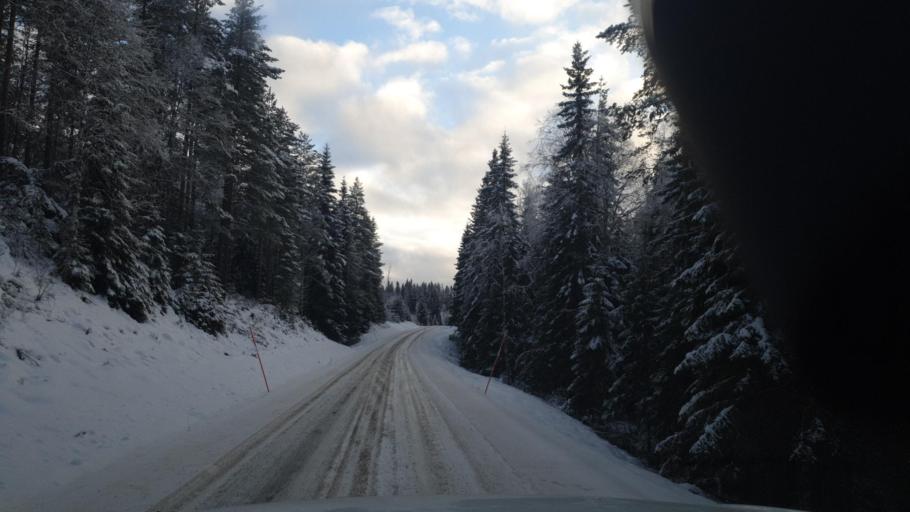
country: SE
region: Vaermland
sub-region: Eda Kommun
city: Charlottenberg
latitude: 60.0938
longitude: 12.6135
